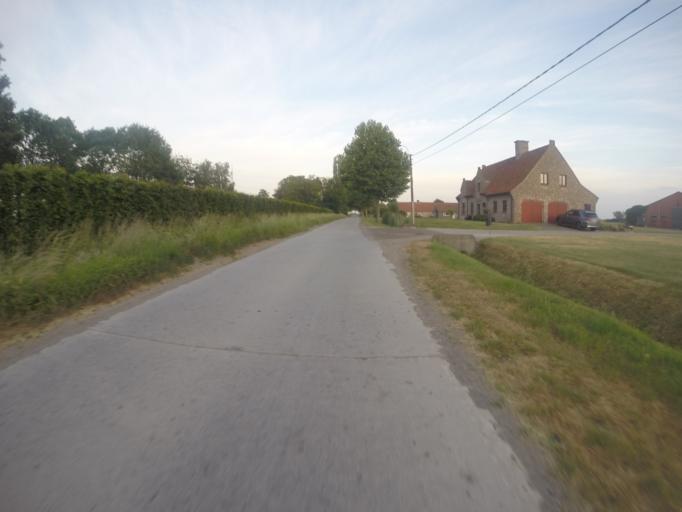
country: BE
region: Flanders
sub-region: Provincie Oost-Vlaanderen
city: Zomergem
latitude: 51.1250
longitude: 3.5272
